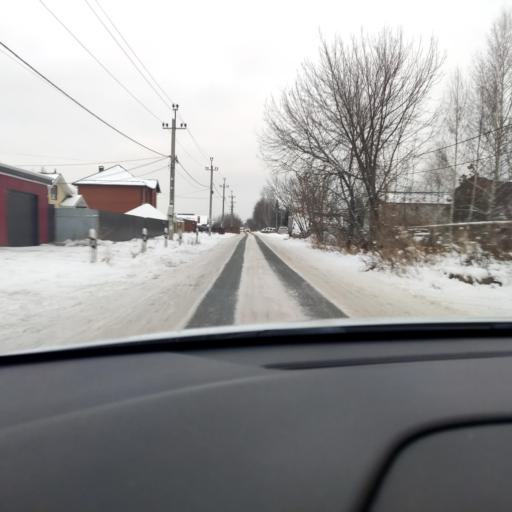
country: RU
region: Tatarstan
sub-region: Gorod Kazan'
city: Kazan
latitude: 55.8715
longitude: 49.1499
